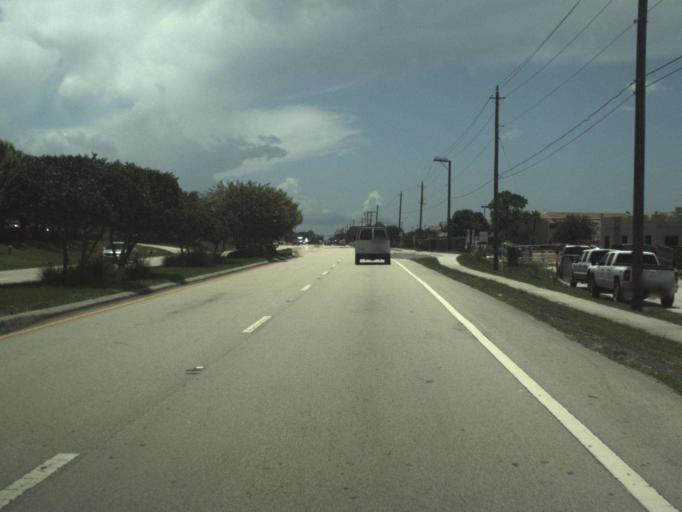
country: US
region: Florida
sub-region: Indian River County
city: Roseland
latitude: 27.8346
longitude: -80.4834
